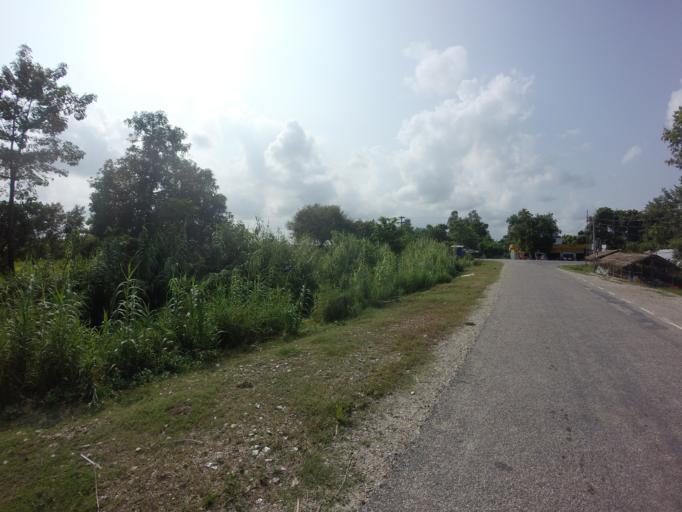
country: NP
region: Far Western
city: Tikapur
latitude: 28.4712
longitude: 81.0705
